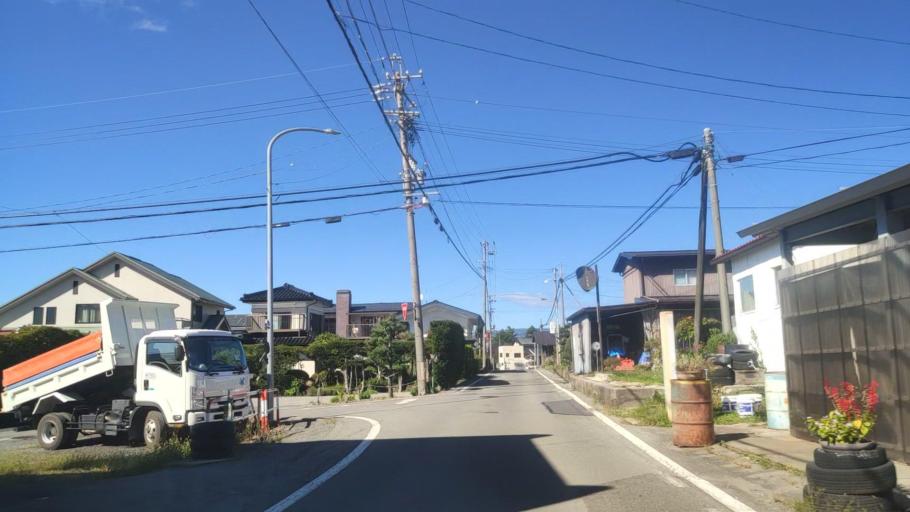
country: JP
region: Nagano
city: Chino
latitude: 35.9670
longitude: 138.2179
